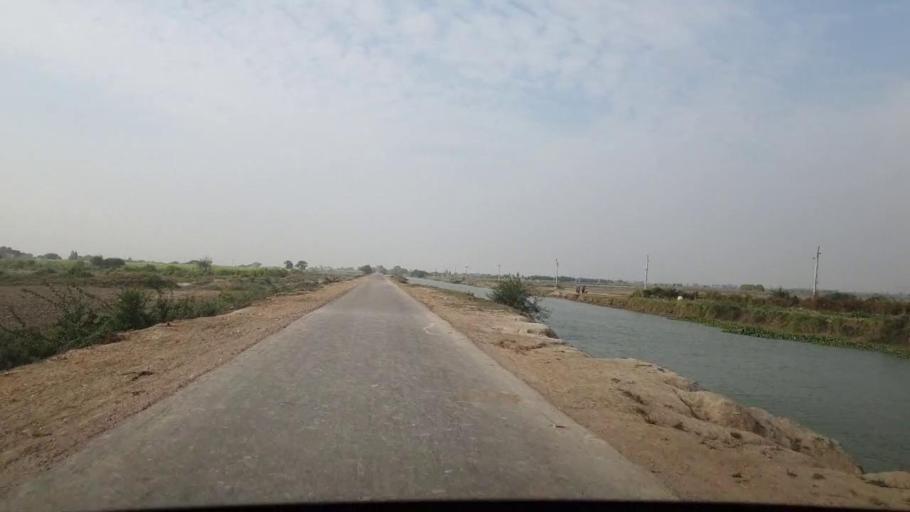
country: PK
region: Sindh
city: Chuhar Jamali
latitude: 24.3937
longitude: 67.9620
